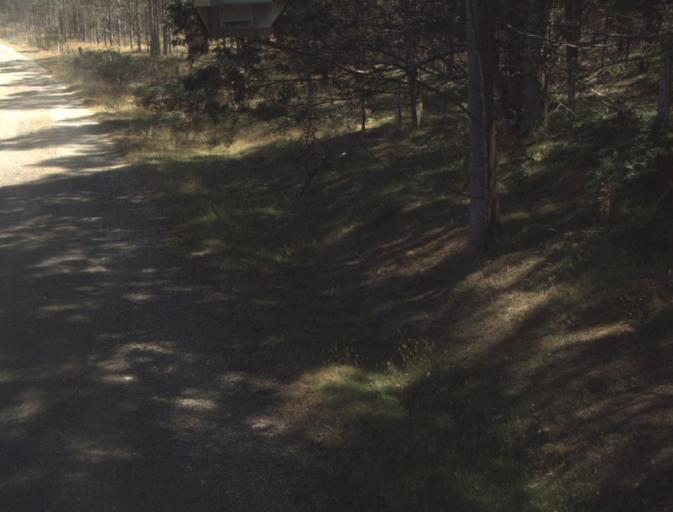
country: AU
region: Tasmania
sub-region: Dorset
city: Scottsdale
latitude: -41.2609
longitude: 147.3501
